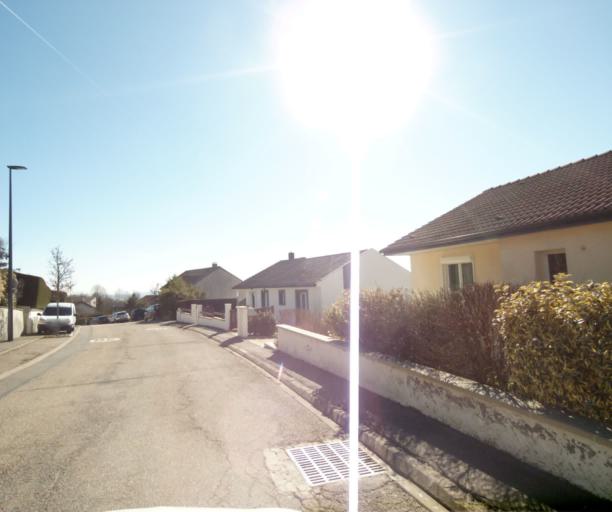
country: FR
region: Lorraine
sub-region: Departement de Meurthe-et-Moselle
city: Essey-les-Nancy
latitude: 48.7130
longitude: 6.2216
